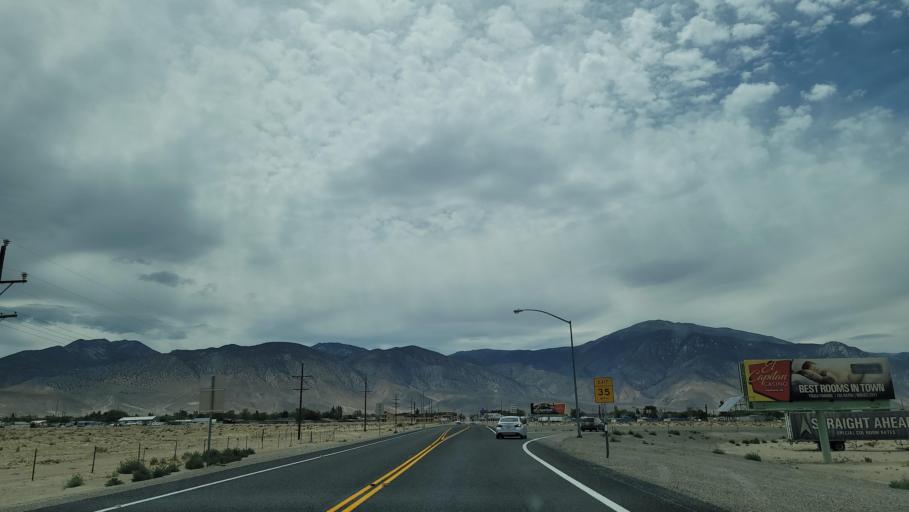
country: US
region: Nevada
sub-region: Mineral County
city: Hawthorne
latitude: 38.5245
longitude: -118.6089
